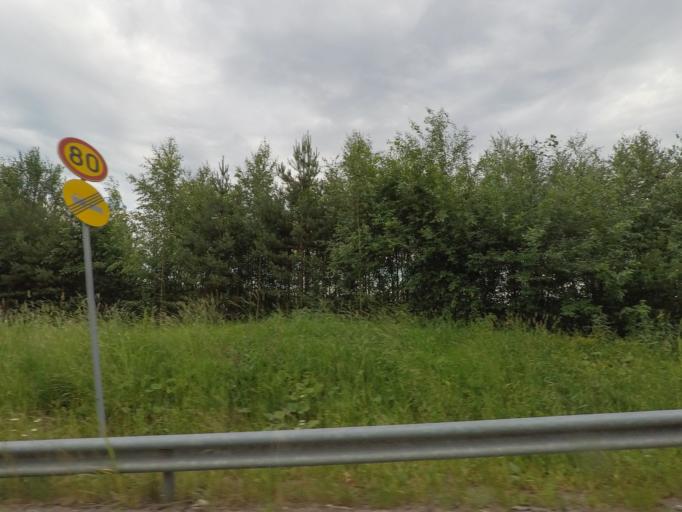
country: FI
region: Uusimaa
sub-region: Helsinki
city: Maentsaelae
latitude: 60.6806
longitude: 25.3608
